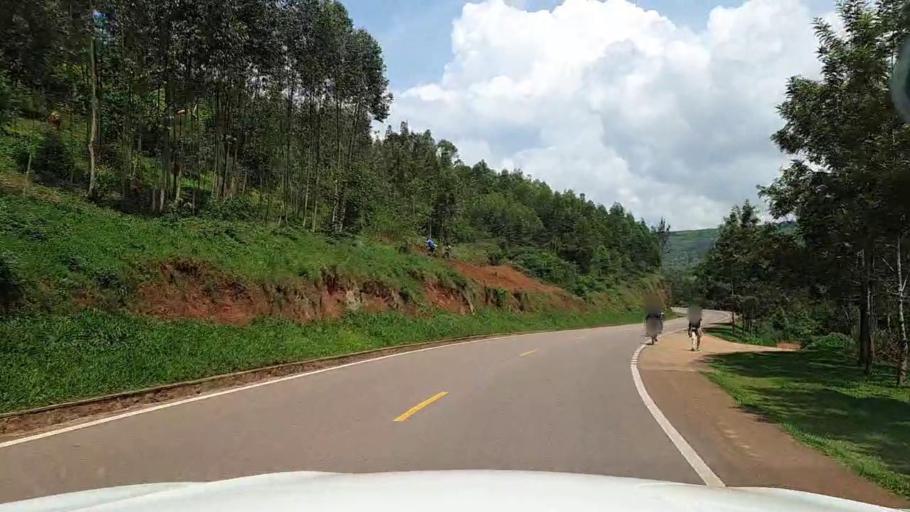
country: RW
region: Kigali
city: Kigali
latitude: -1.8316
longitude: 30.0786
